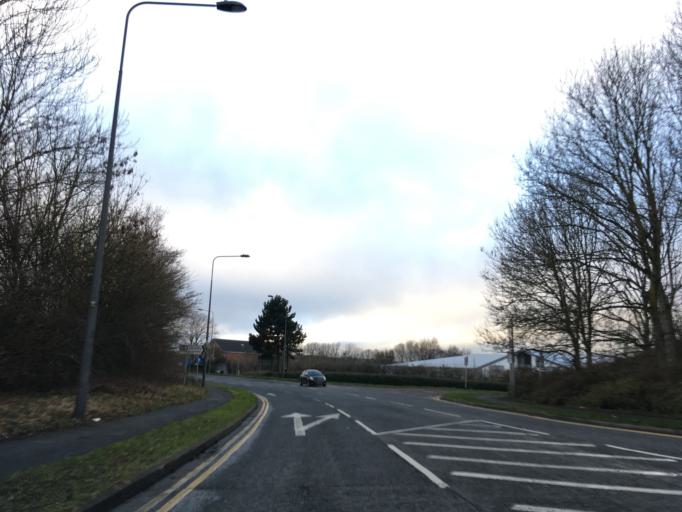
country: GB
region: England
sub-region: South Gloucestershire
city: Stoke Gifford
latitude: 51.5107
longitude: -2.5513
